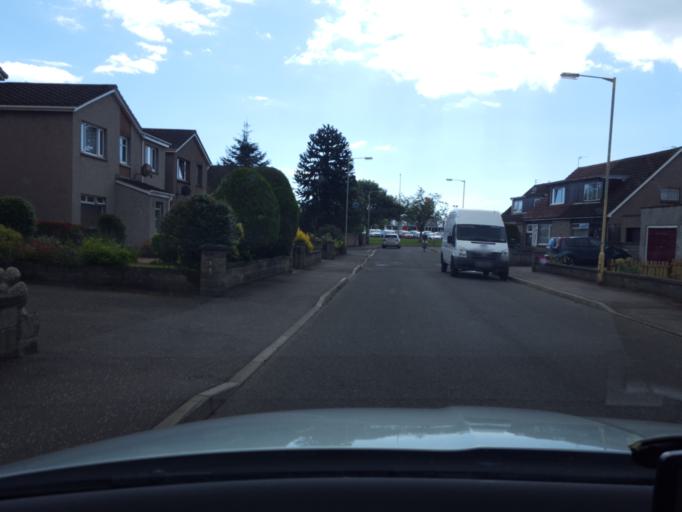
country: GB
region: Scotland
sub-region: Angus
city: Arbroath
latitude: 56.5725
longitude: -2.5783
